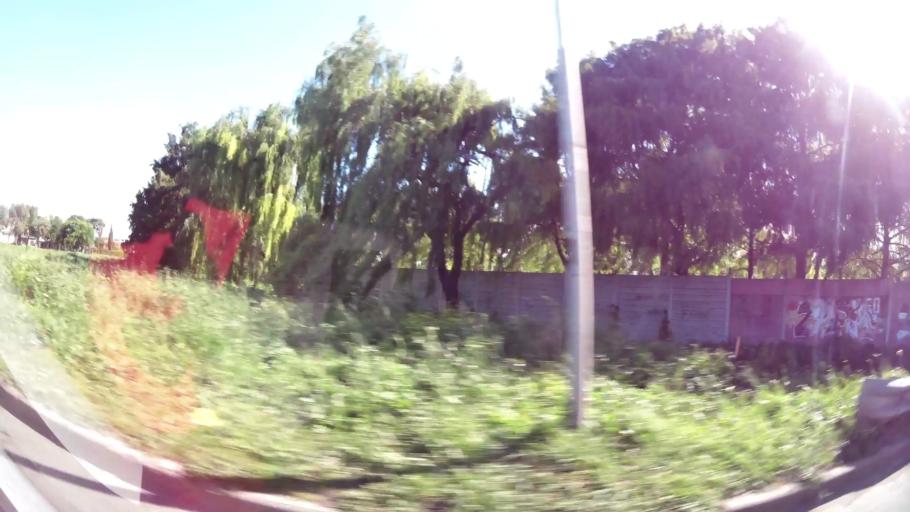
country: AR
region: Buenos Aires
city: Santa Catalina - Dique Lujan
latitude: -34.4671
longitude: -58.6922
